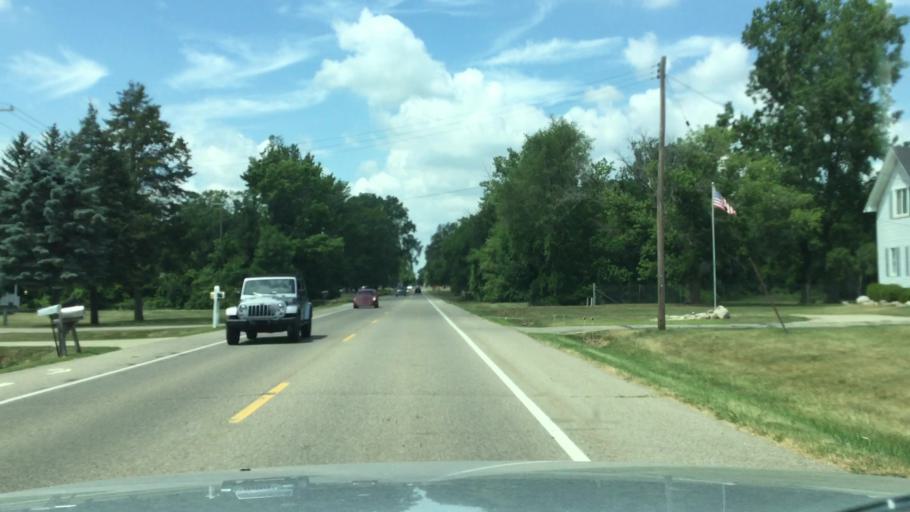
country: US
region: Michigan
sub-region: Genesee County
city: Flushing
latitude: 43.0674
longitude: -83.8198
